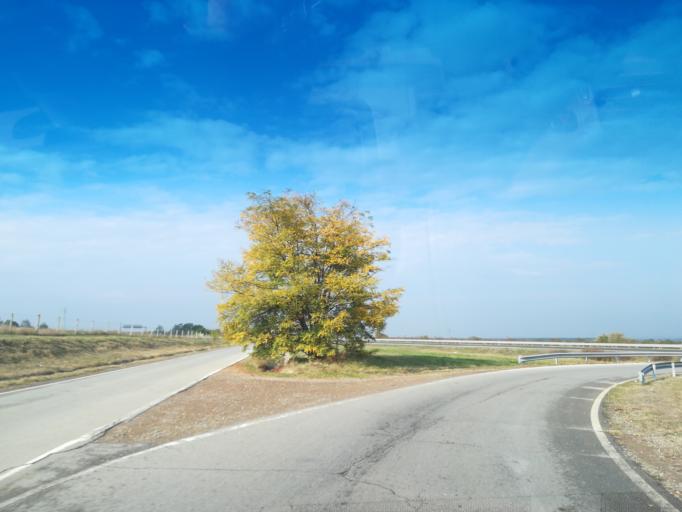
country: BG
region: Stara Zagora
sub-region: Obshtina Chirpan
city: Chirpan
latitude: 42.2064
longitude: 25.3017
